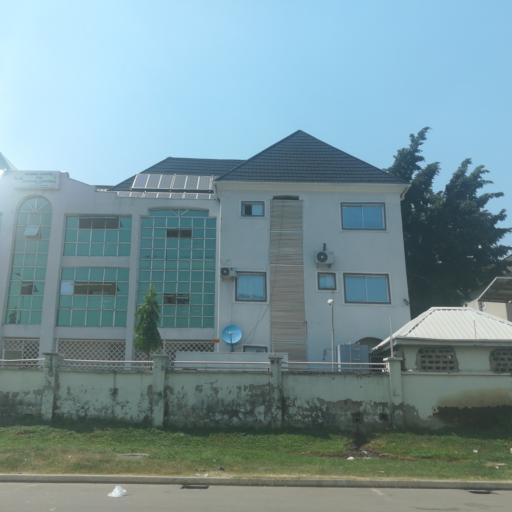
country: NG
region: Abuja Federal Capital Territory
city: Abuja
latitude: 9.0709
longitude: 7.4336
